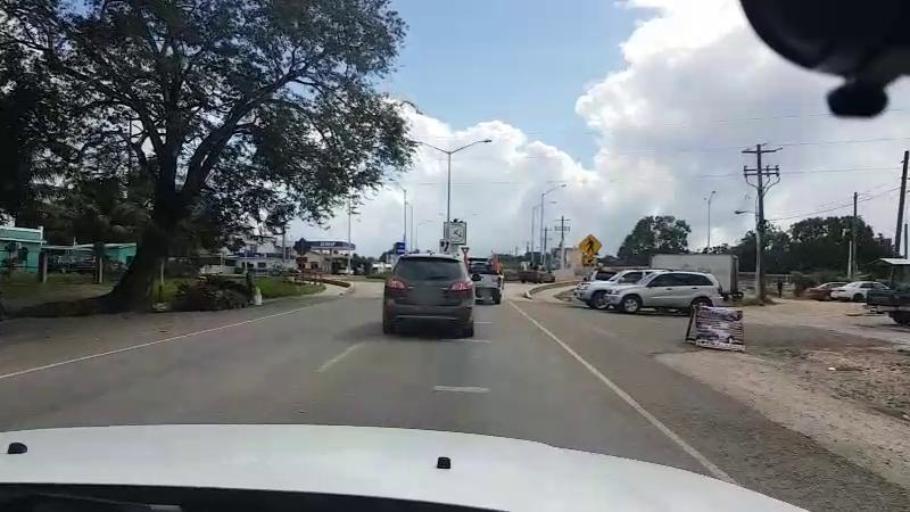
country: BZ
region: Cayo
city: Belmopan
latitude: 17.2511
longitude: -88.7850
